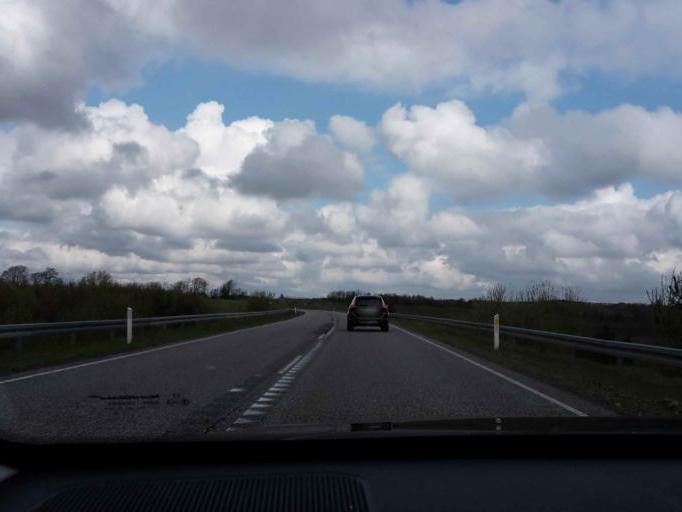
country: DK
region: South Denmark
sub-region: Billund Kommune
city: Billund
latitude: 55.7373
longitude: 9.2034
